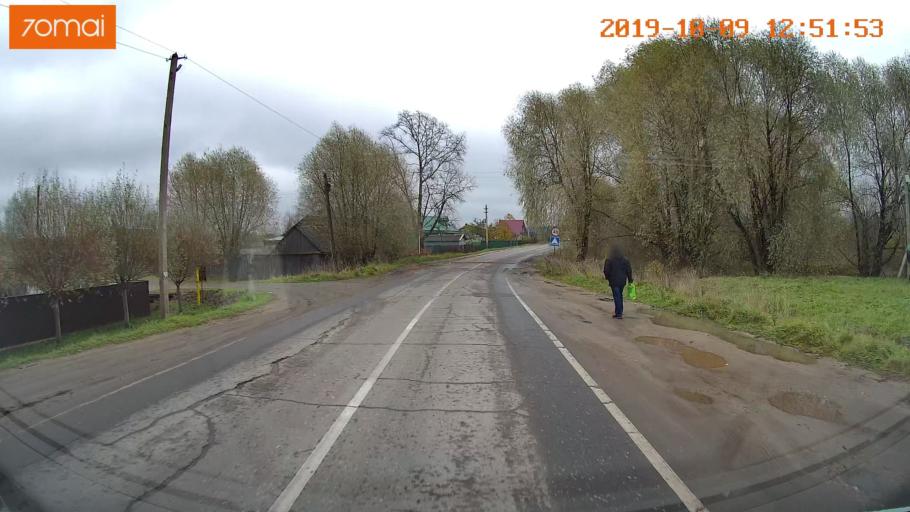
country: RU
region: Jaroslavl
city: Prechistoye
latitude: 58.4170
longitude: 40.3478
